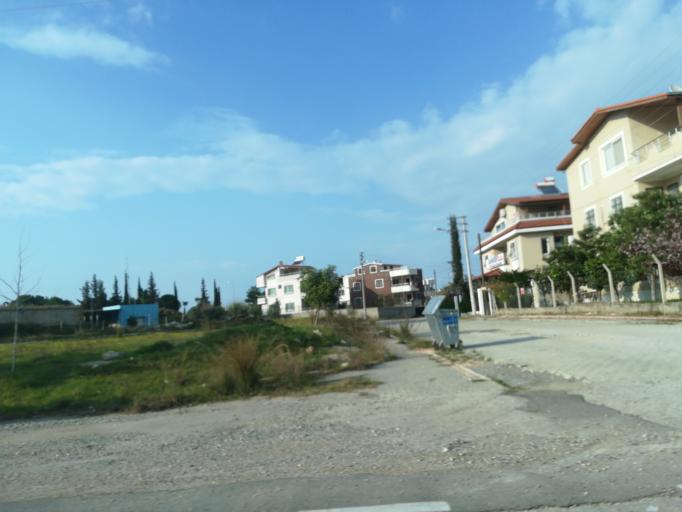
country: TR
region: Adana
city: Adana
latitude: 37.0779
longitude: 35.3893
